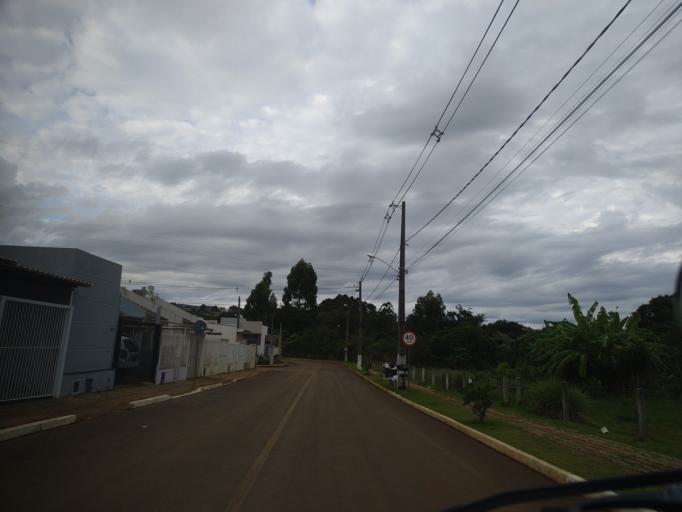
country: BR
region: Santa Catarina
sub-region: Chapeco
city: Chapeco
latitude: -27.0632
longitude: -52.6153
